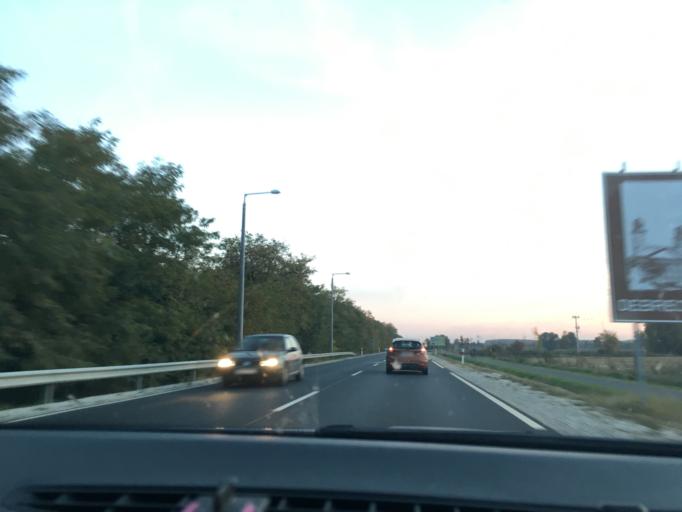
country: HU
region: Hajdu-Bihar
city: Hajduhadhaz
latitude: 47.6337
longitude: 21.6593
